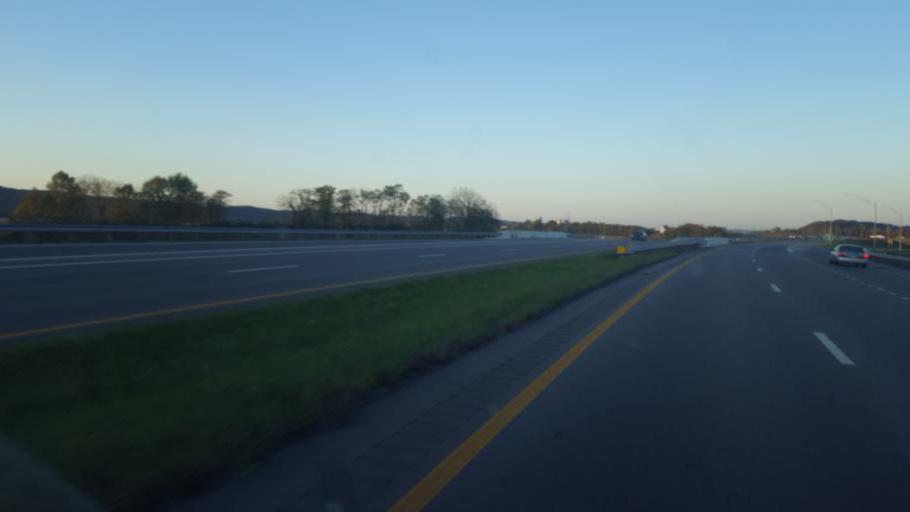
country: US
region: Ohio
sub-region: Pike County
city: Piketon
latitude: 39.0443
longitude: -83.0266
